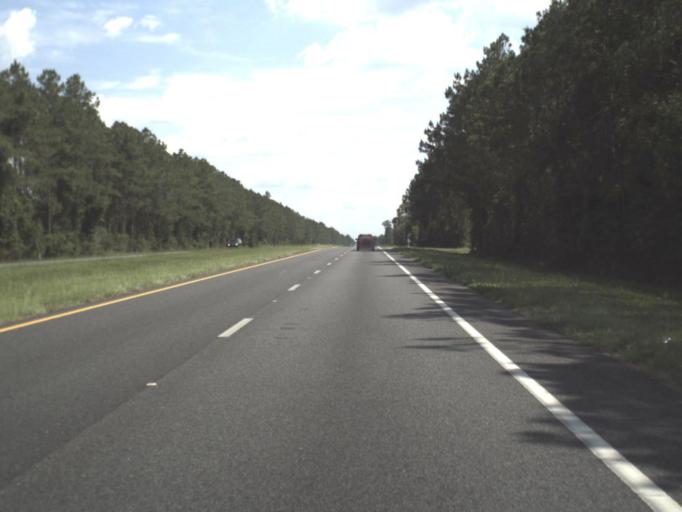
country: US
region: Florida
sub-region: Alachua County
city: Waldo
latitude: 29.7478
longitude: -82.1413
